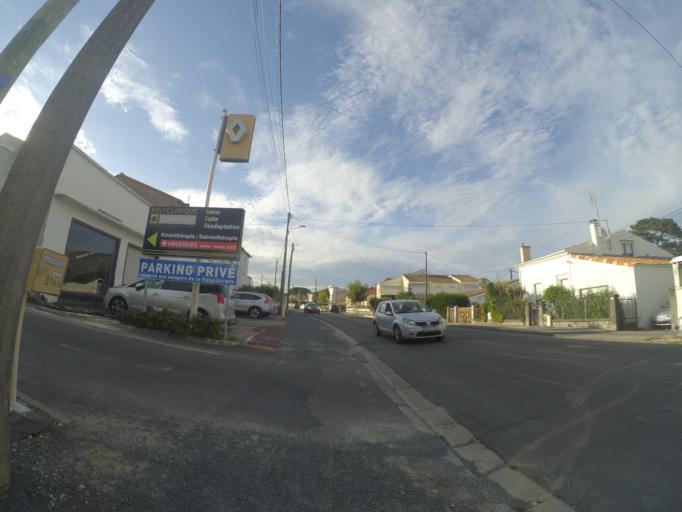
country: FR
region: Poitou-Charentes
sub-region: Departement de la Charente-Maritime
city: Saint-Georges-de-Didonne
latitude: 45.6030
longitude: -1.0030
